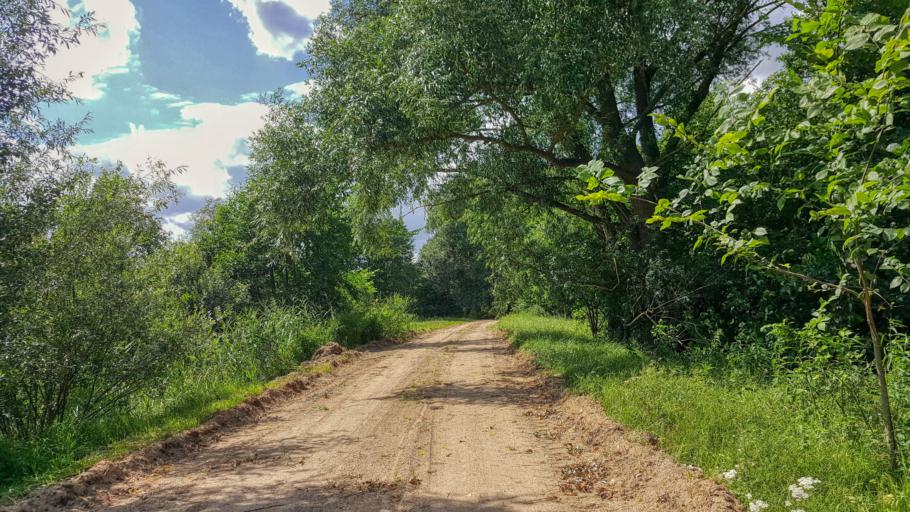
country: BY
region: Brest
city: Kamyanyets
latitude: 52.4241
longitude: 23.8728
